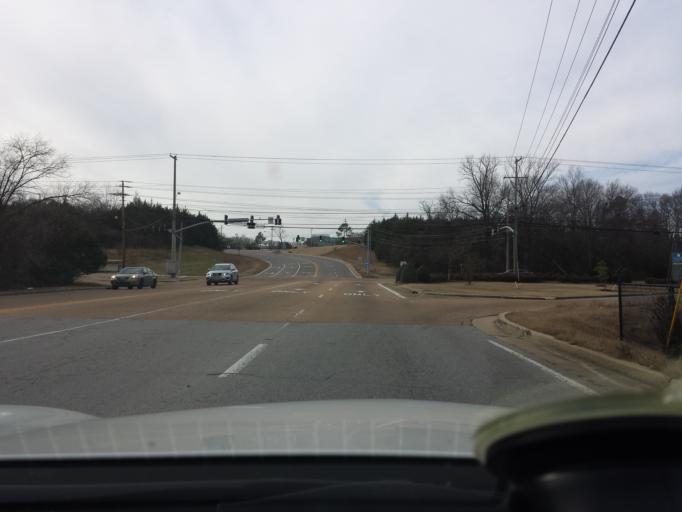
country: US
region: Mississippi
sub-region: Lee County
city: Tupelo
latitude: 34.2361
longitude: -88.7101
